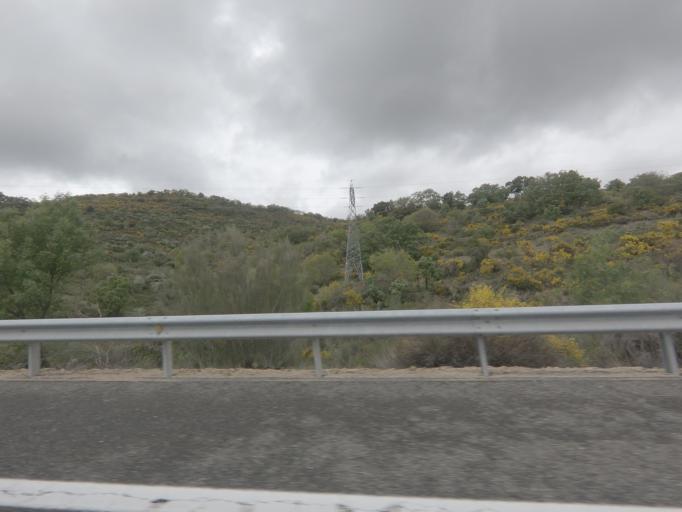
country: ES
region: Extremadura
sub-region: Provincia de Caceres
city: Hervas
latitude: 40.2937
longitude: -5.8961
